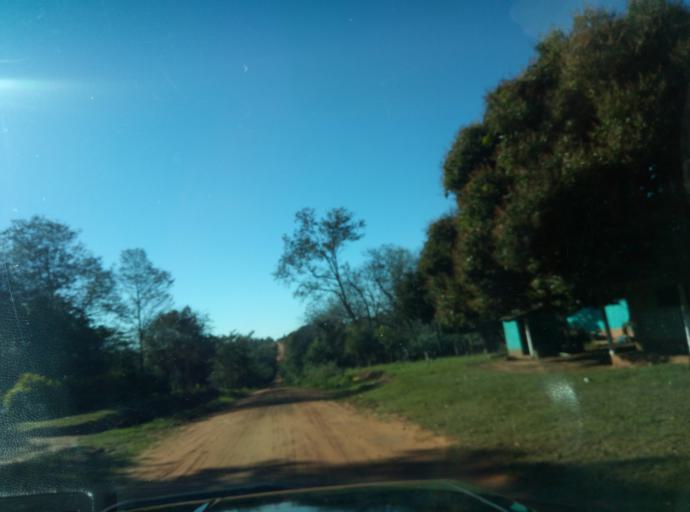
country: PY
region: Caaguazu
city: Carayao
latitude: -25.1586
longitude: -56.2918
